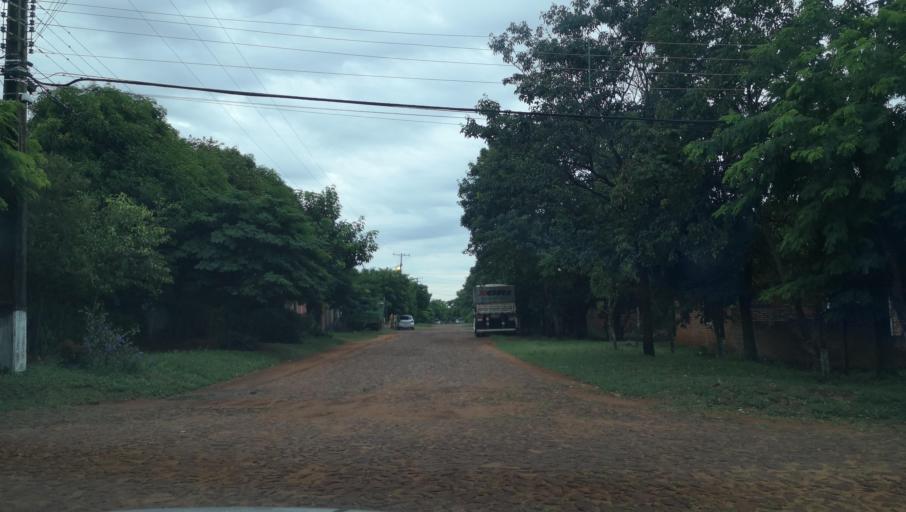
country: PY
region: Misiones
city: Santa Maria
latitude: -26.8891
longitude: -57.0397
